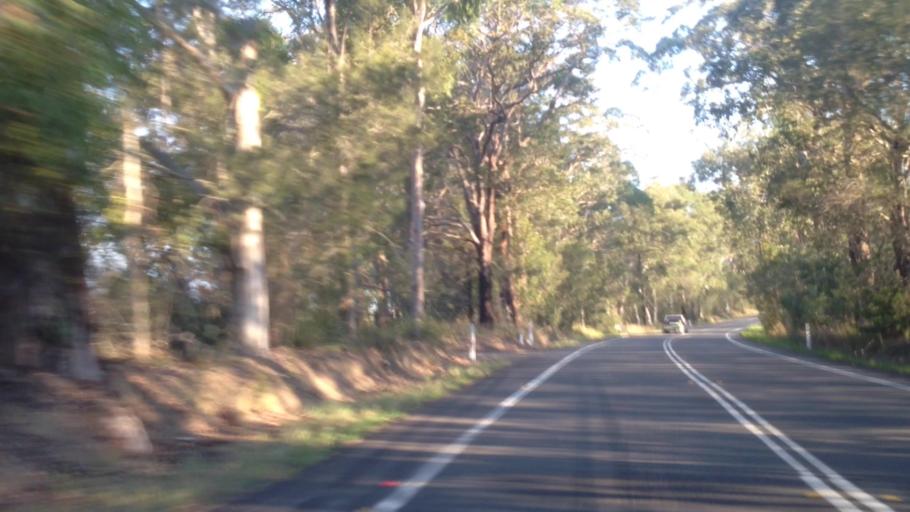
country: AU
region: New South Wales
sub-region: Lake Macquarie Shire
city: Dora Creek
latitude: -33.0220
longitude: 151.4943
